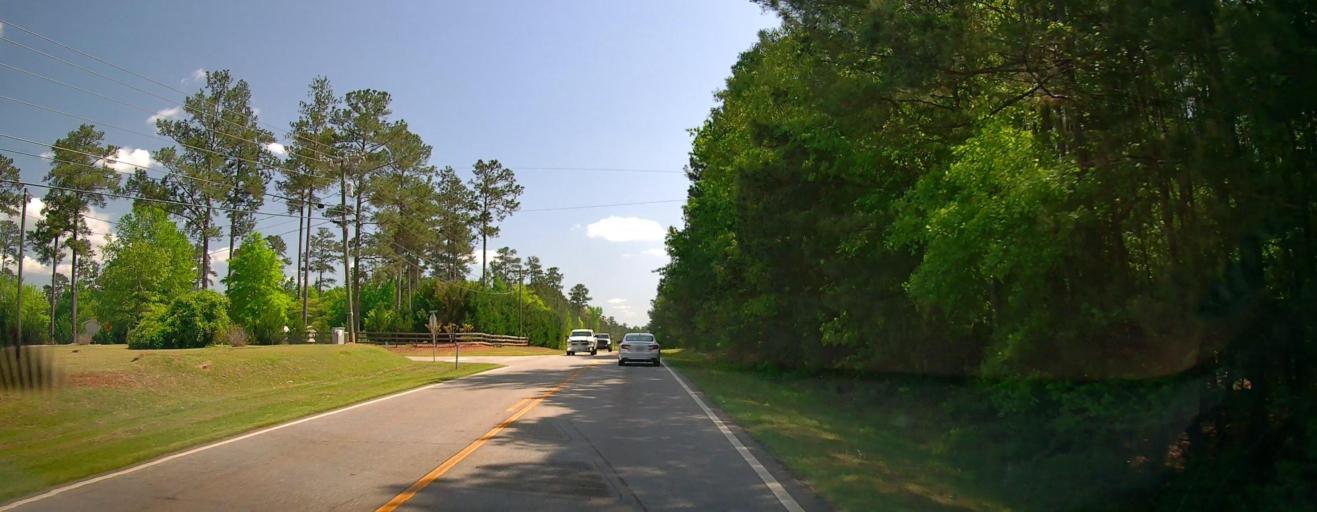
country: US
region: Georgia
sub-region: Putnam County
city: Eatonton
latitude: 33.2635
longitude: -83.3012
